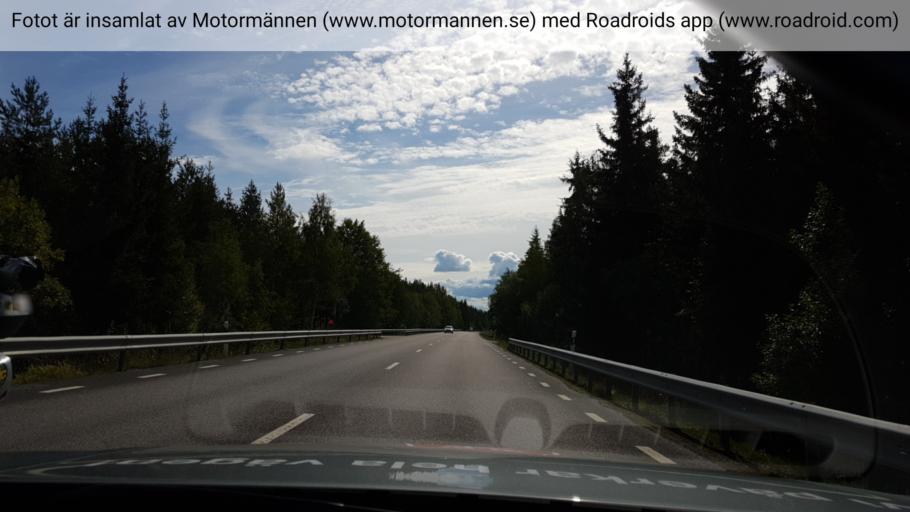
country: SE
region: Uppsala
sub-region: Osthammars Kommun
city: Bjorklinge
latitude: 59.9658
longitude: 17.3820
